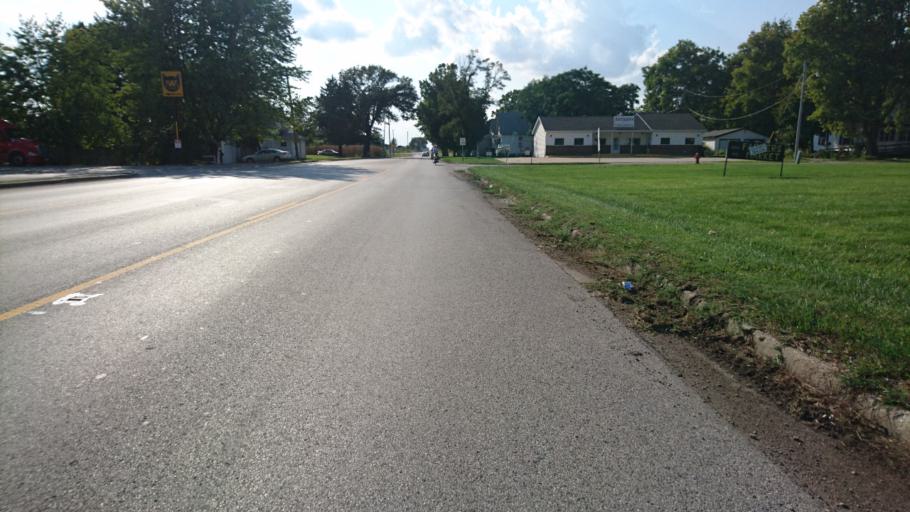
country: US
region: Illinois
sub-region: Logan County
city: Atlanta
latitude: 40.3116
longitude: -89.1694
